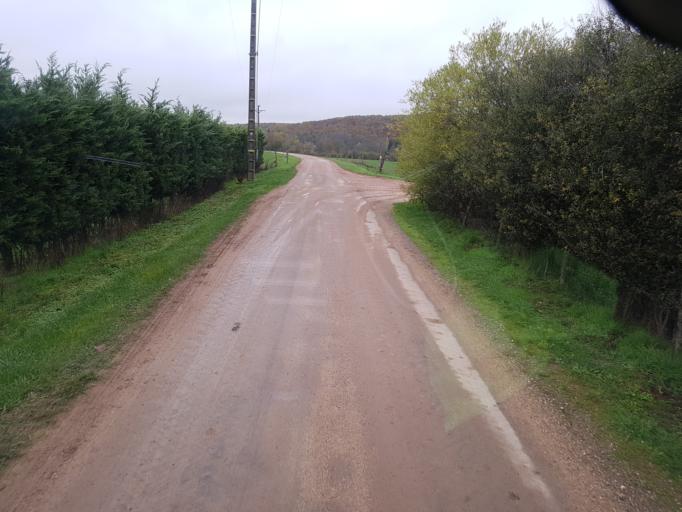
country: FR
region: Bourgogne
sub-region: Departement de la Cote-d'Or
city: Is-sur-Tille
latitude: 47.5346
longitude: 4.9817
